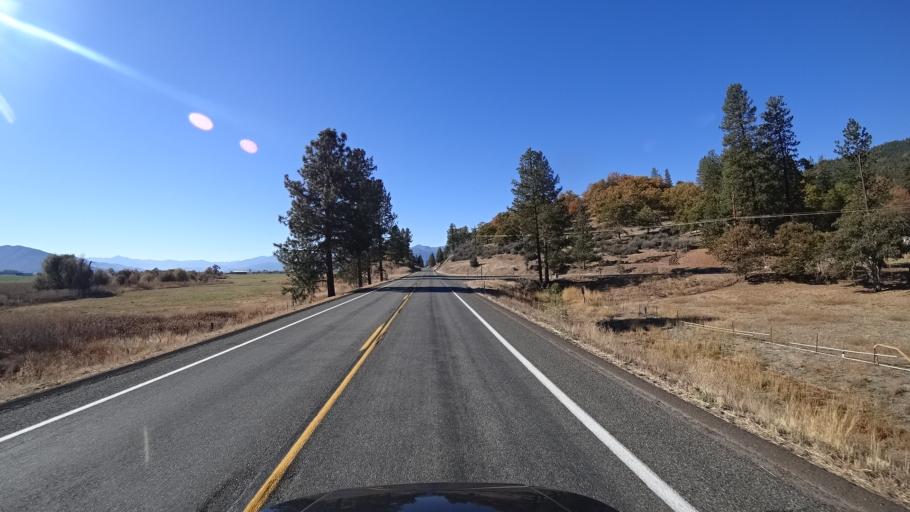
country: US
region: California
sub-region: Siskiyou County
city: Yreka
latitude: 41.5890
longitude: -122.8575
